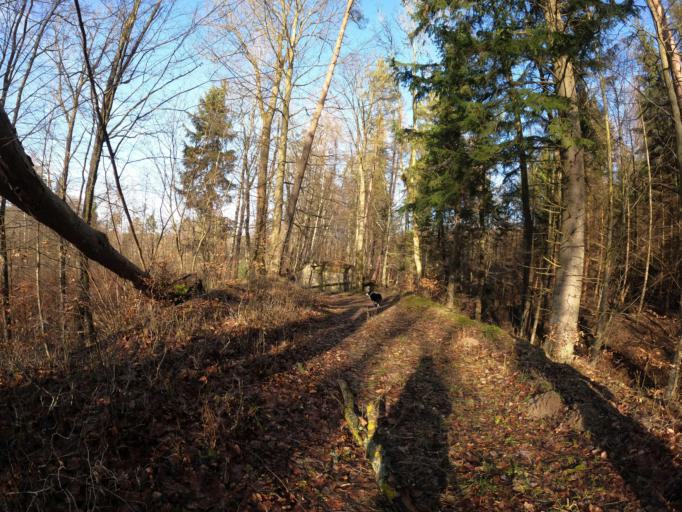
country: PL
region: West Pomeranian Voivodeship
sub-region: Powiat koszalinski
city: Polanow
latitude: 54.2078
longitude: 16.7202
